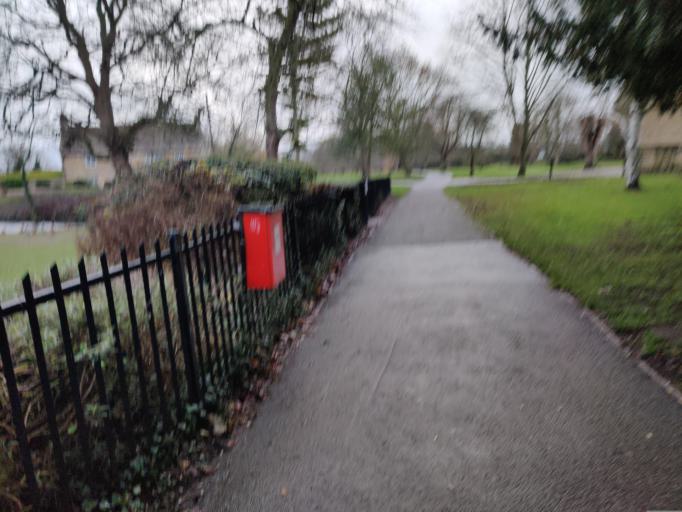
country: GB
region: England
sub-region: Lincolnshire
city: Bourne
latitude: 52.7670
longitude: -0.3778
